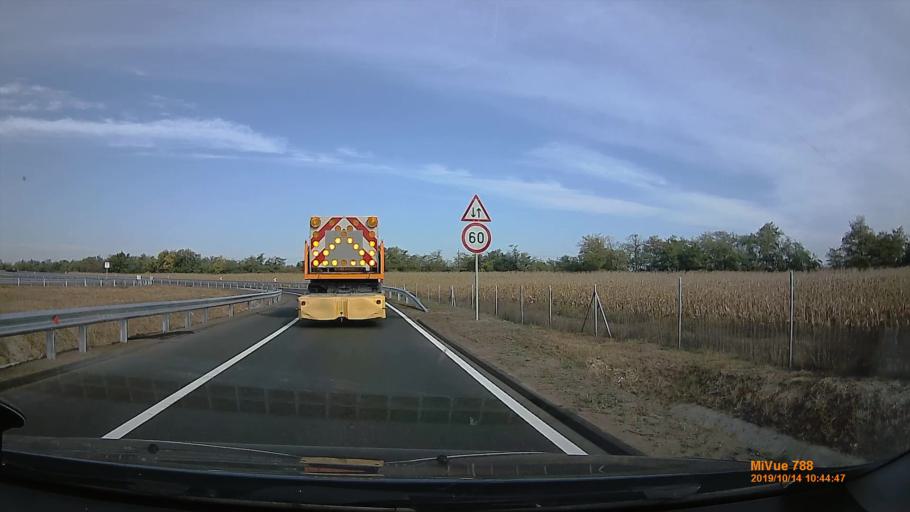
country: HU
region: Pest
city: Albertirsa
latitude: 47.2642
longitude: 19.6203
